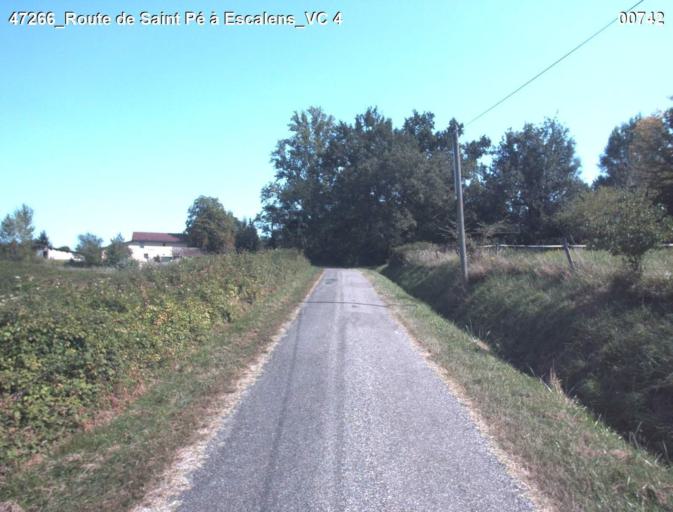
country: FR
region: Aquitaine
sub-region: Departement des Landes
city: Gabarret
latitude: 44.0022
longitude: 0.0694
